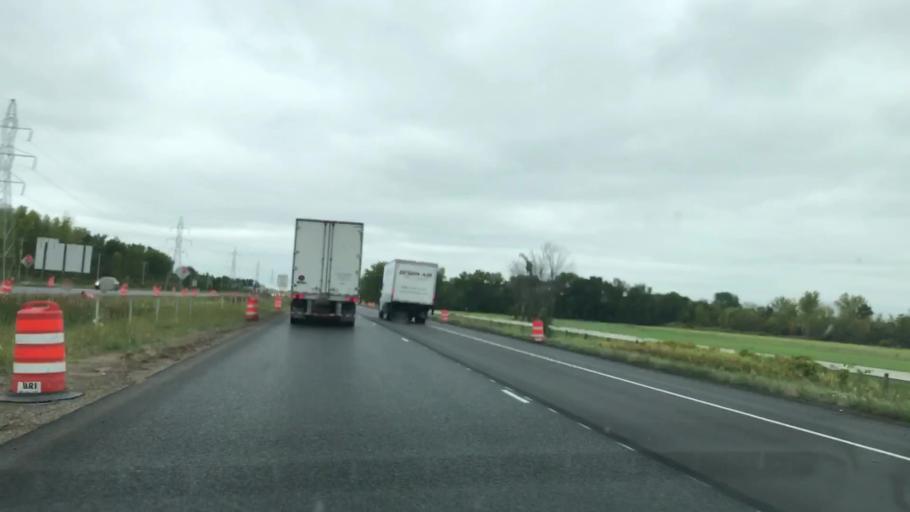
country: US
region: Wisconsin
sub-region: Brown County
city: Suamico
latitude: 44.6178
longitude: -88.0501
